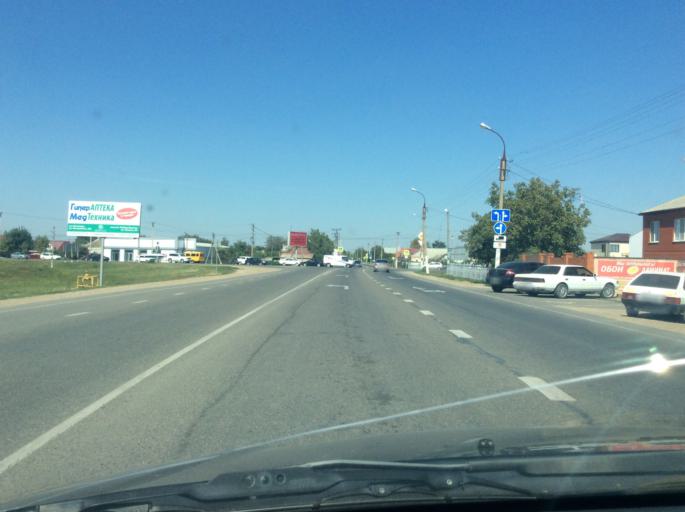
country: RU
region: Krasnodarskiy
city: Slavyansk-na-Kubani
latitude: 45.2484
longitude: 38.1007
